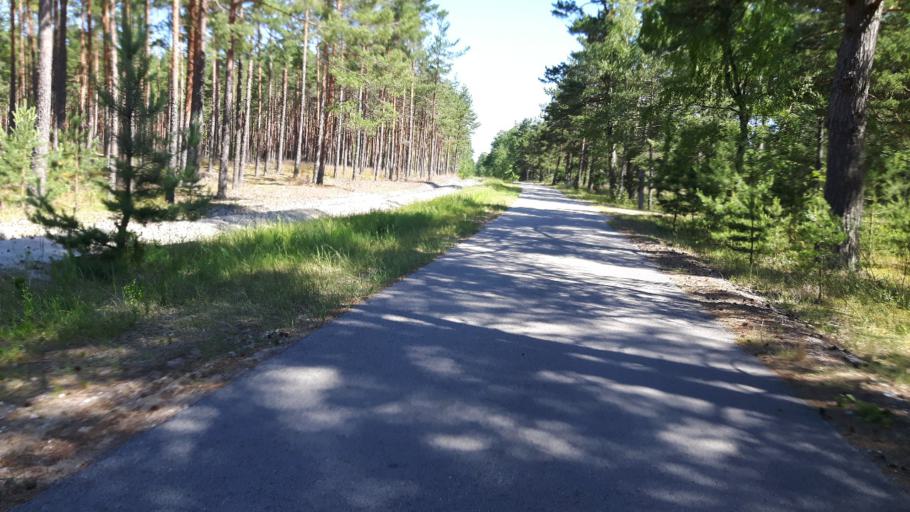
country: LT
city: Nida
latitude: 55.3316
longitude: 21.0324
